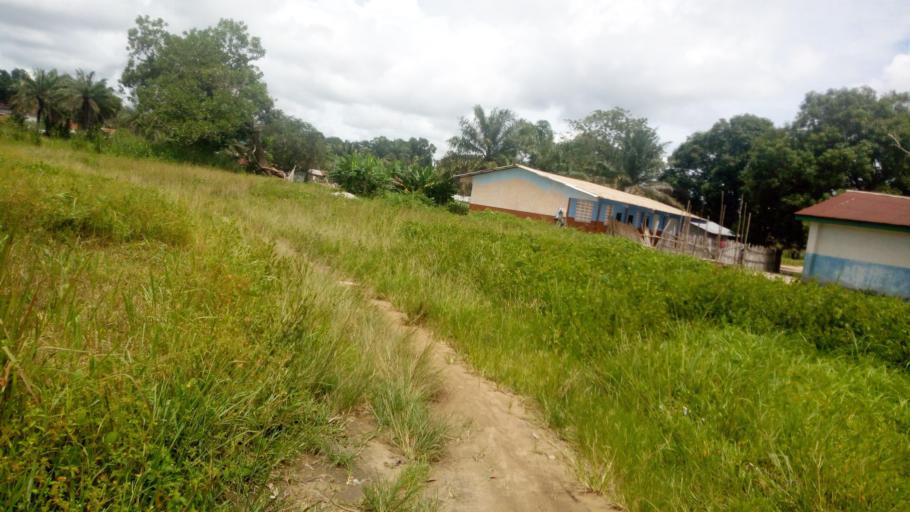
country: SL
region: Northern Province
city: Magburaka
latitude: 8.7201
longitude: -11.9470
